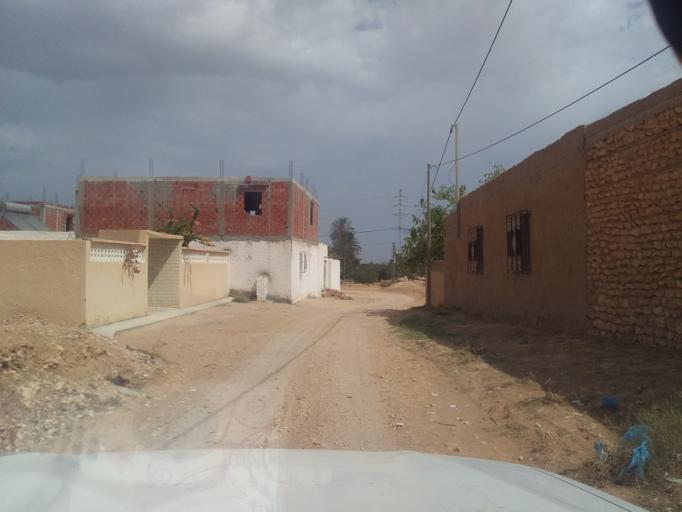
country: TN
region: Madanin
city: Medenine
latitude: 33.5918
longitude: 10.3261
